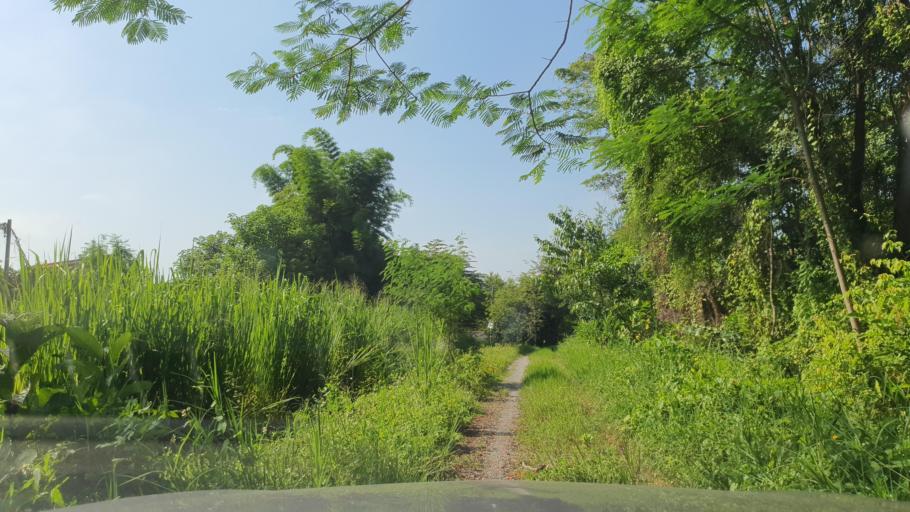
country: TH
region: Chiang Mai
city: Hang Dong
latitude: 18.7198
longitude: 98.9314
